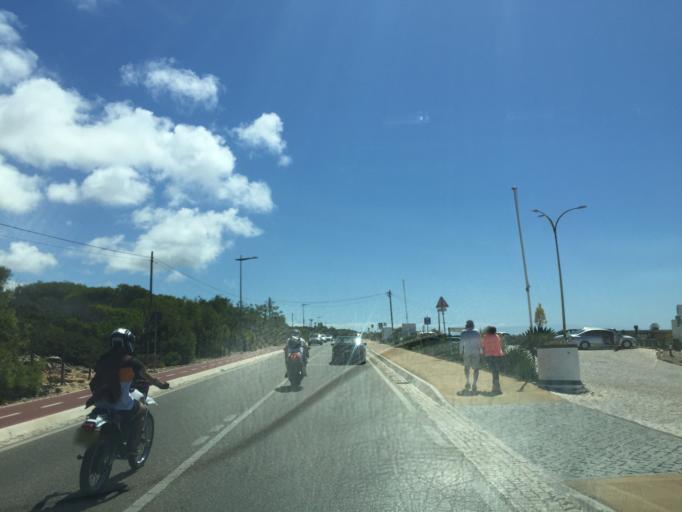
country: PT
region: Lisbon
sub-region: Cascais
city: Cascais
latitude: 38.7016
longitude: -9.4724
